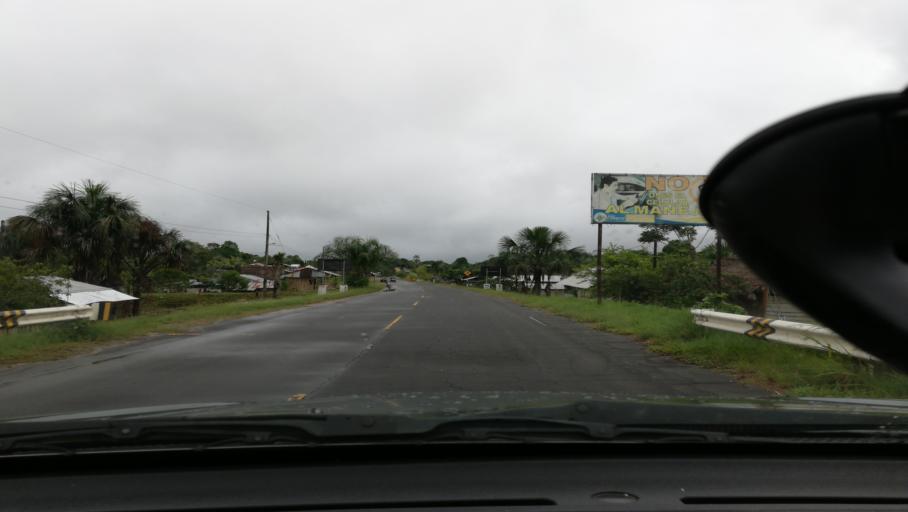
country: PE
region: Loreto
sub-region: Provincia de Loreto
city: Nauta
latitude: -4.2218
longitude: -73.4825
